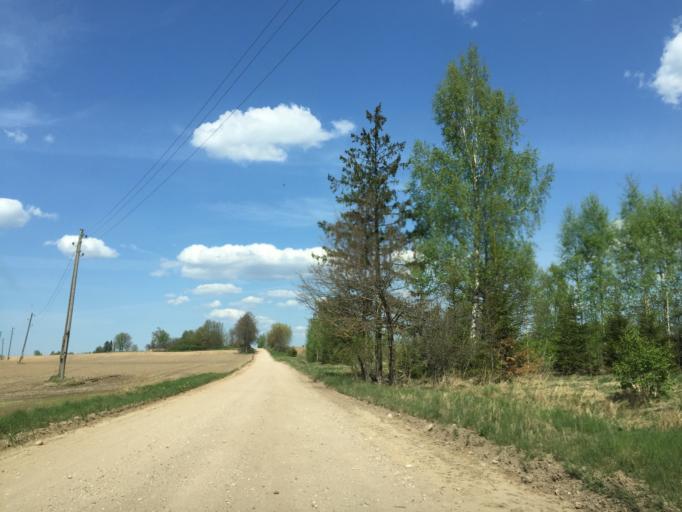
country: LV
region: Krimulda
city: Ragana
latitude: 57.3453
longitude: 24.6525
